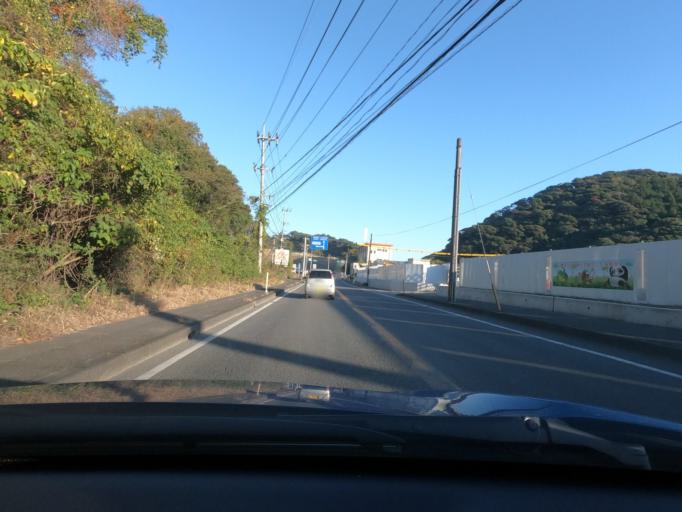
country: JP
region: Kagoshima
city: Satsumasendai
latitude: 31.8470
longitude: 130.2701
